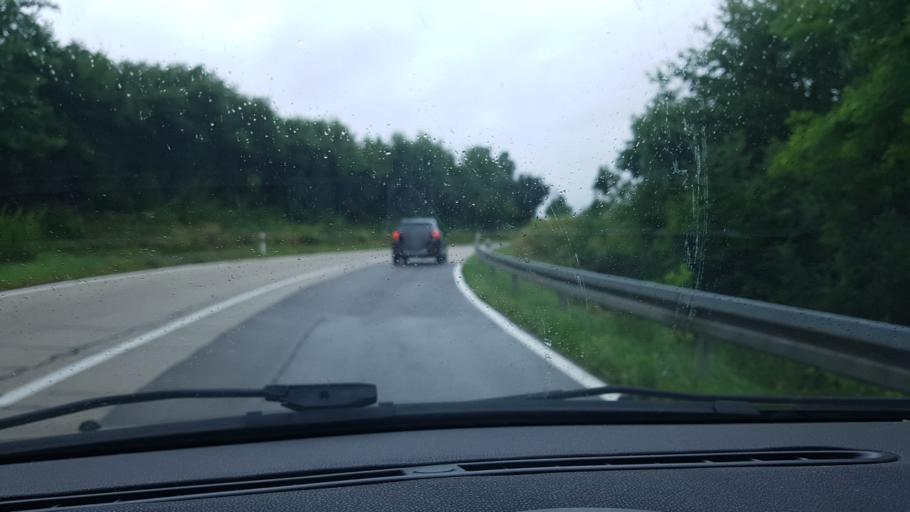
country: HR
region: Karlovacka
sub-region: Grad Karlovac
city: Karlovac
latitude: 45.4546
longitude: 15.4383
